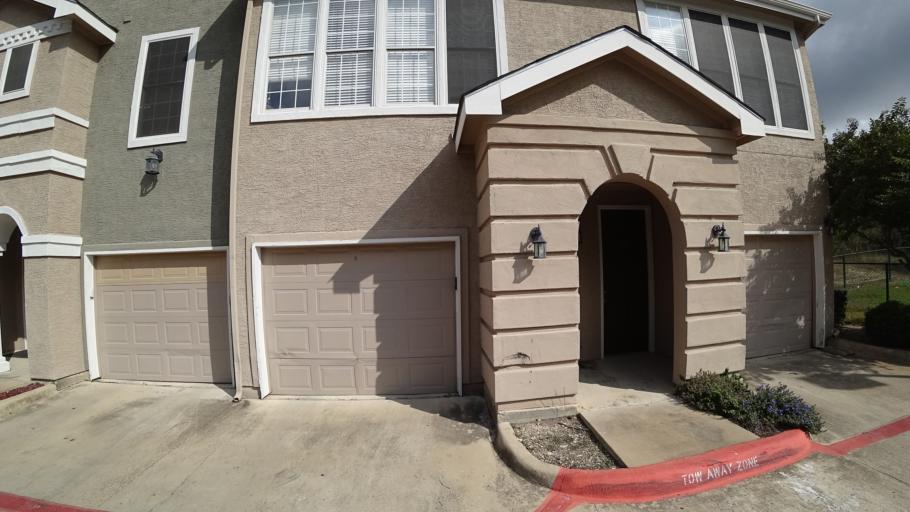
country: US
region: Texas
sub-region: Travis County
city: Hudson Bend
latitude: 30.3823
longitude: -97.8796
